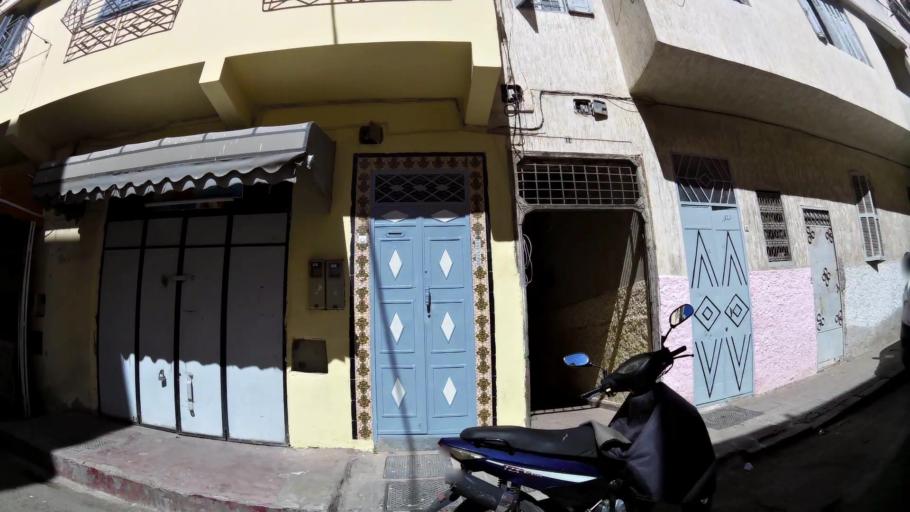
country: MA
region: Meknes-Tafilalet
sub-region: Meknes
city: Meknes
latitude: 33.8875
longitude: -5.5708
